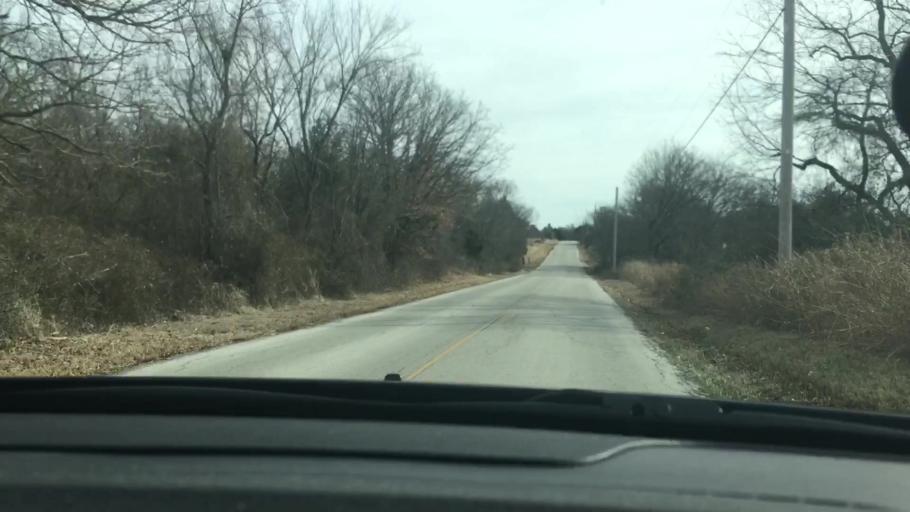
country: US
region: Oklahoma
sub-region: Carter County
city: Ardmore
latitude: 34.1748
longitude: -97.0843
